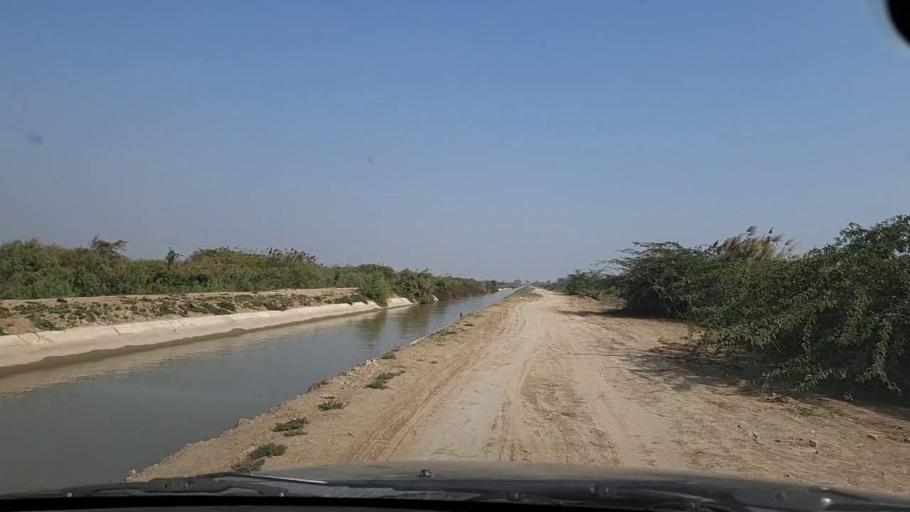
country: PK
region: Sindh
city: Mirpur Sakro
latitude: 24.3419
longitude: 67.7153
